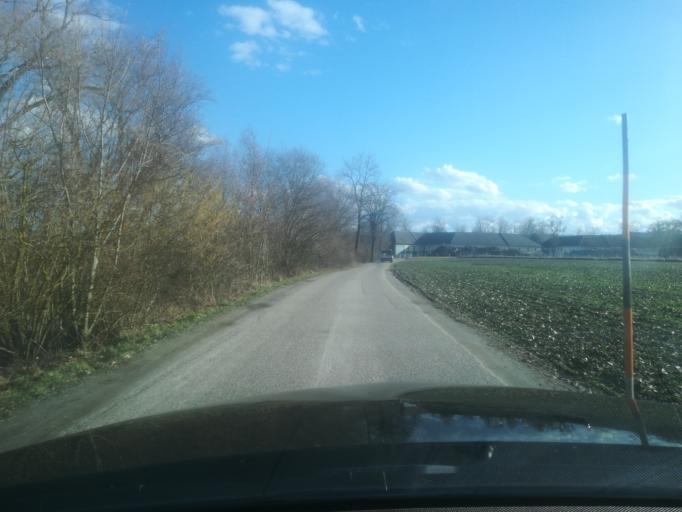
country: AT
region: Upper Austria
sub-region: Wels-Land
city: Buchkirchen
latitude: 48.2860
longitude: 14.0152
